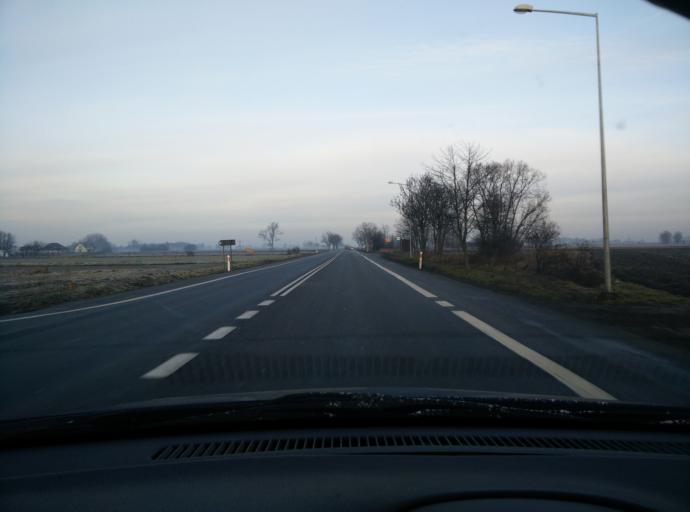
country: PL
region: Greater Poland Voivodeship
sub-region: Powiat poznanski
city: Kornik
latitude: 52.2382
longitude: 17.1584
